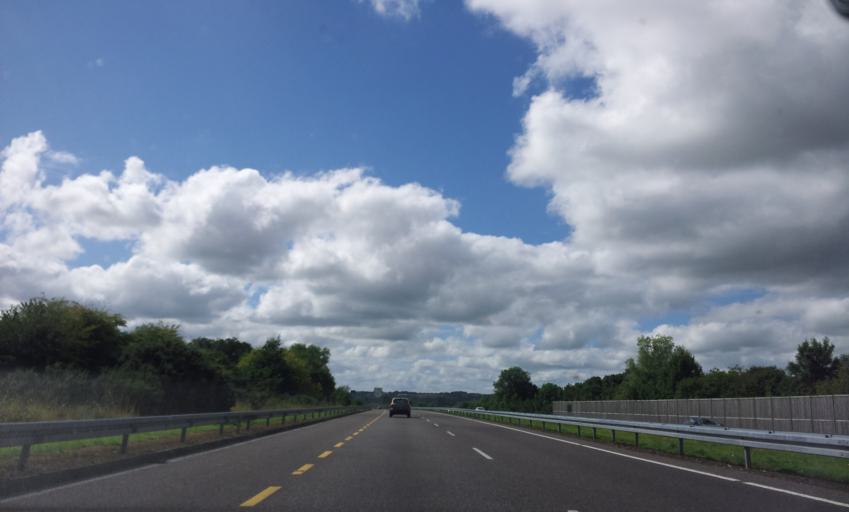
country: IE
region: Munster
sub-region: County Cork
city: Killumney
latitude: 51.8782
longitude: -8.6231
